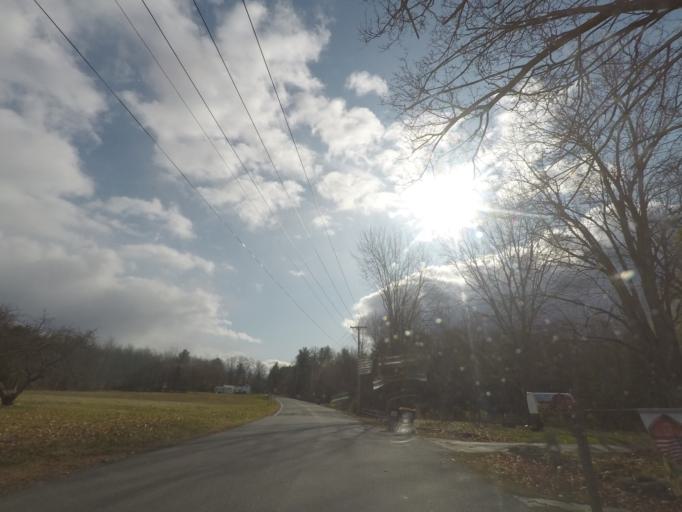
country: US
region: New York
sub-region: Saratoga County
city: Country Knolls
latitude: 42.9217
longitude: -73.8363
